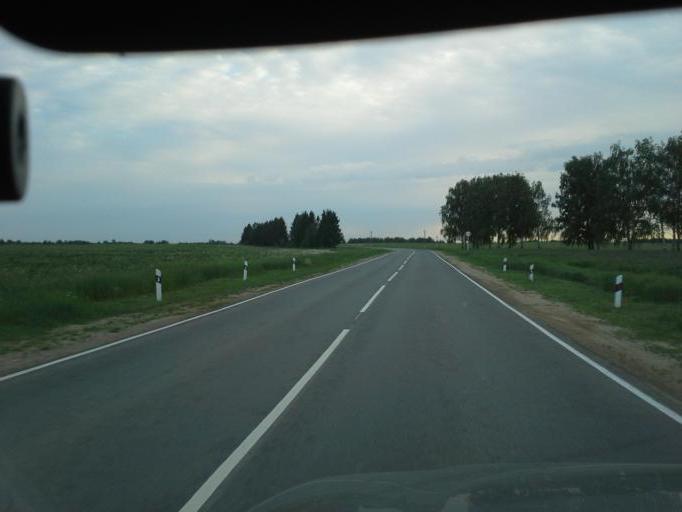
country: RU
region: Ivanovo
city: Gavrilov Posad
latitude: 56.5824
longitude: 40.2142
